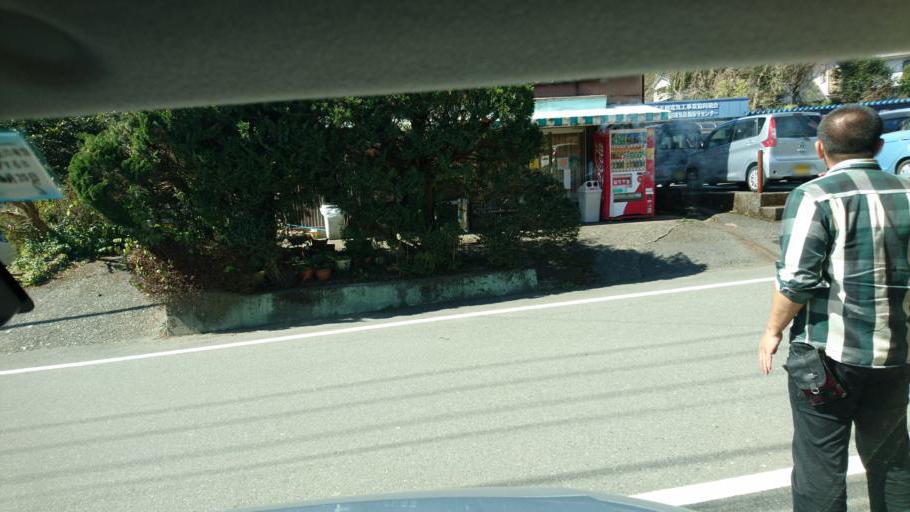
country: JP
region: Oita
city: Takedamachi
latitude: 32.7124
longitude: 131.3094
